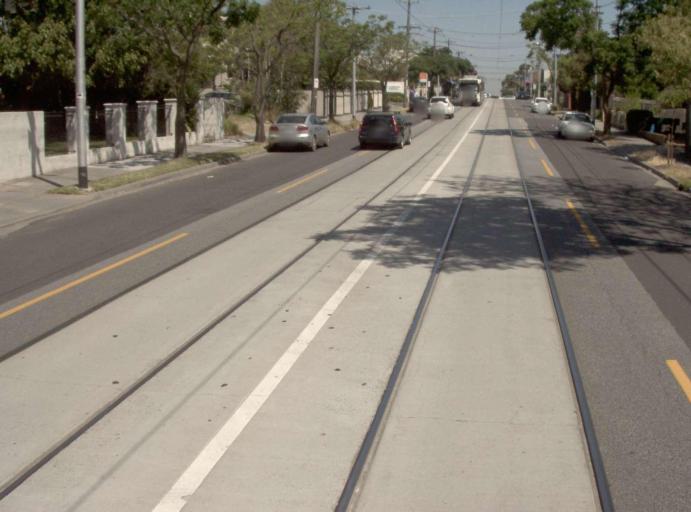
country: AU
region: Victoria
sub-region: Boroondara
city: Hawthorn East
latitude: -37.8290
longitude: 145.0366
